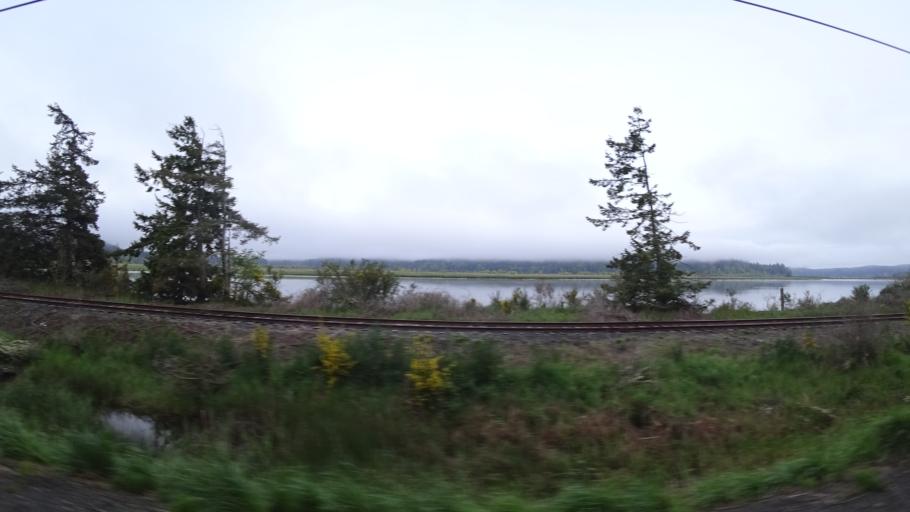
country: US
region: Oregon
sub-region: Douglas County
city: Reedsport
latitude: 43.7238
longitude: -124.1094
